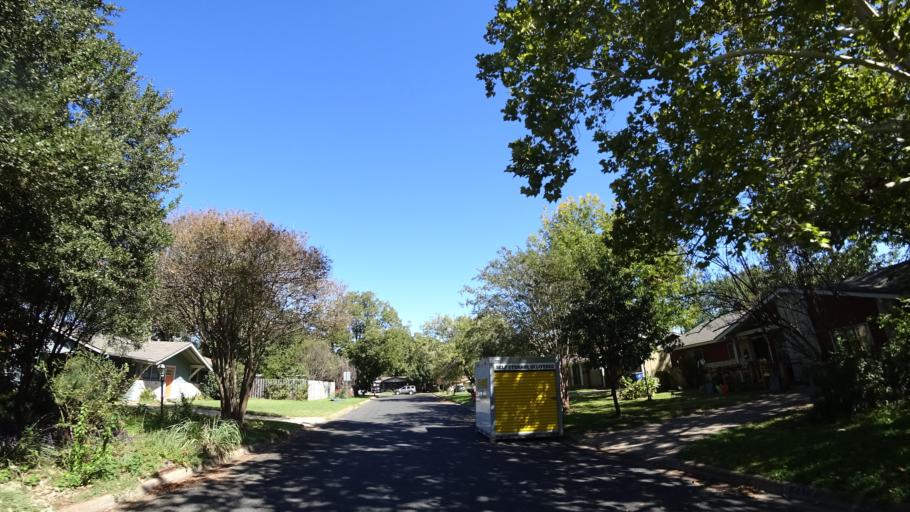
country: US
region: Texas
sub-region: Travis County
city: Rollingwood
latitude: 30.2213
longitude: -97.7882
